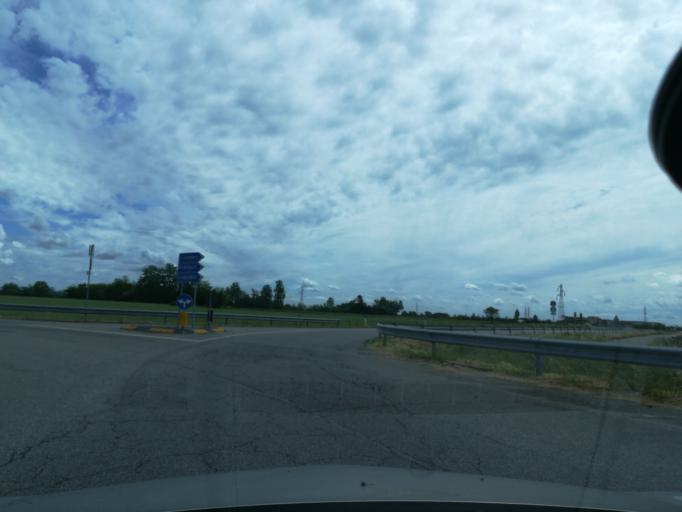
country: IT
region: Lombardy
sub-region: Provincia di Bergamo
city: Cividate al Piano
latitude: 45.5393
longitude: 9.8286
